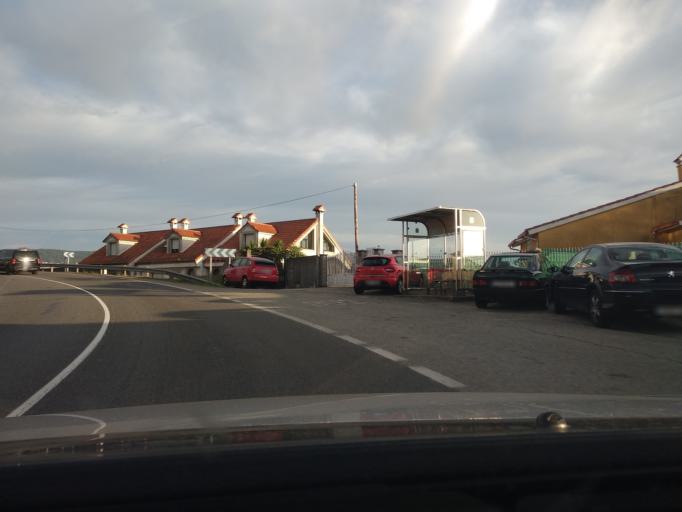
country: ES
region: Galicia
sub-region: Provincia de Pontevedra
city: Moana
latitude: 42.2807
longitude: -8.7108
